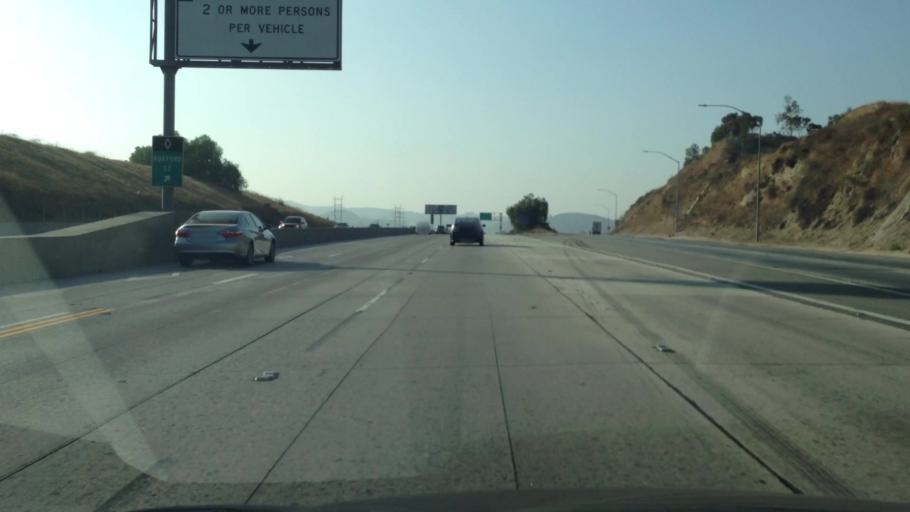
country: US
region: California
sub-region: Los Angeles County
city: San Fernando
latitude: 34.2892
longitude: -118.4655
